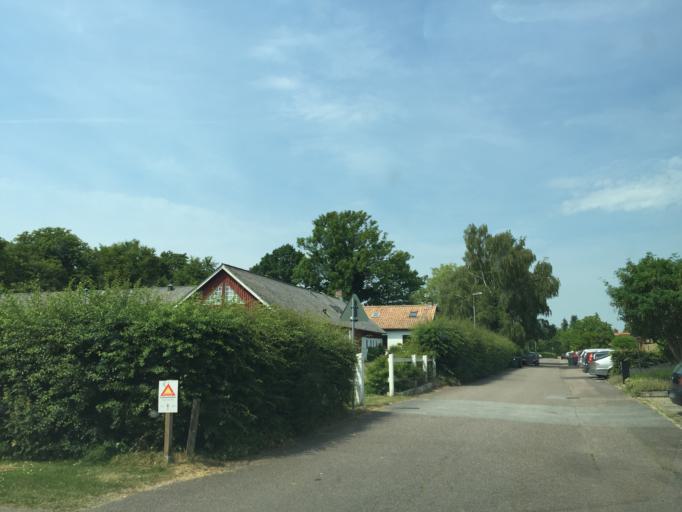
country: SE
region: Skane
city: Bjarred
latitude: 55.7128
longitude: 13.0320
